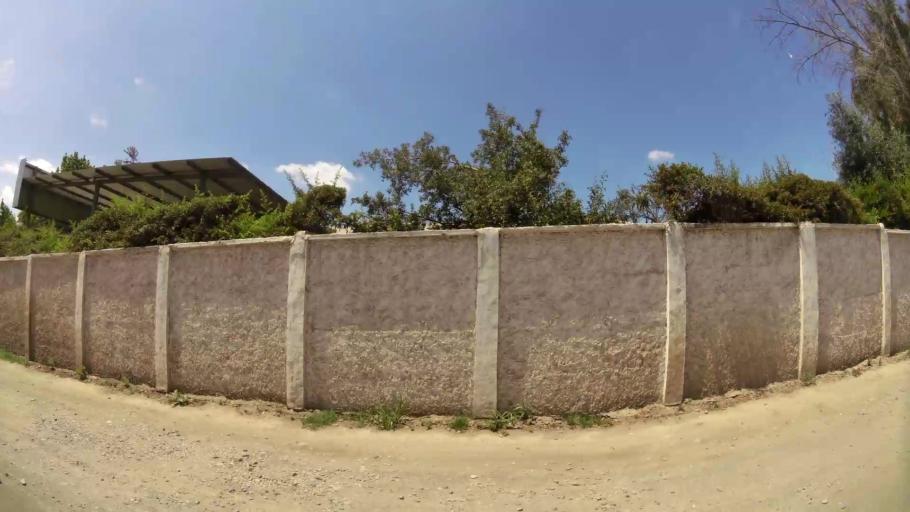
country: CL
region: Santiago Metropolitan
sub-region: Provincia de Talagante
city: Penaflor
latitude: -33.5683
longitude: -70.7945
